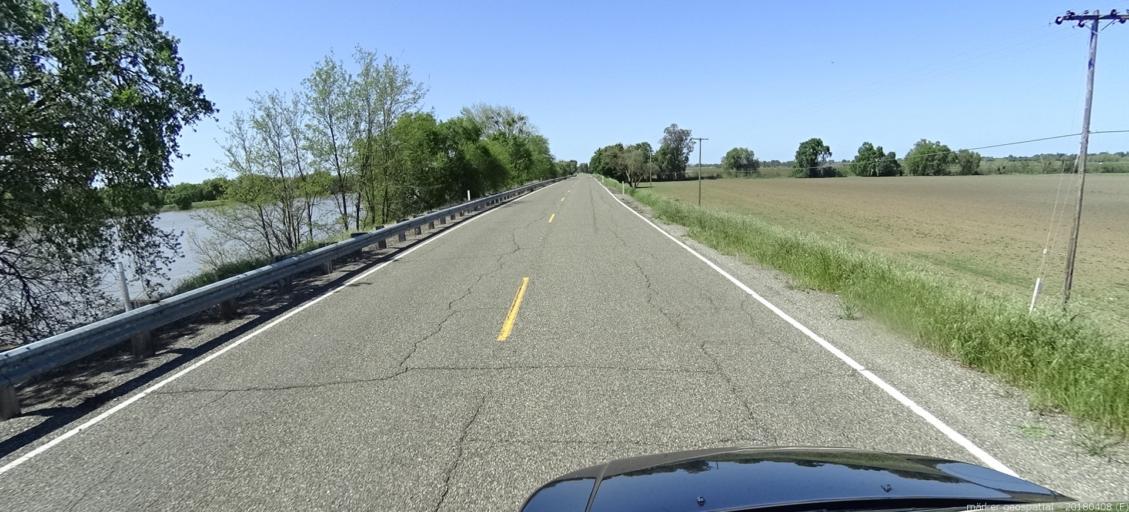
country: US
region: California
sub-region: Sacramento County
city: Laguna
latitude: 38.4121
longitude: -121.5181
